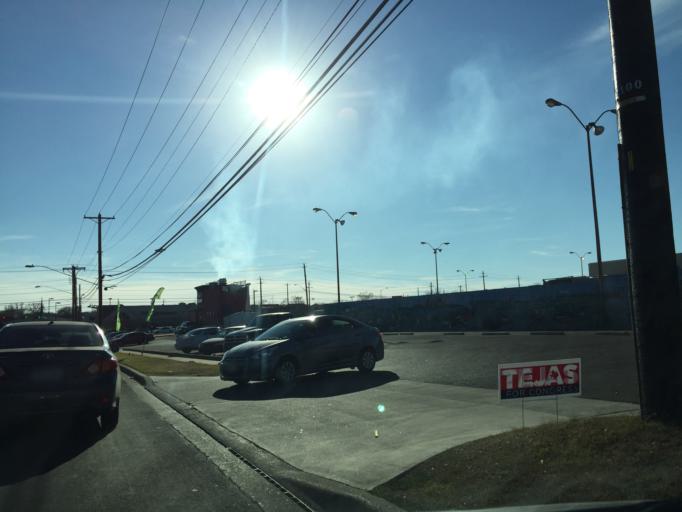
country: US
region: Texas
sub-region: Travis County
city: Rollingwood
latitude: 30.2094
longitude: -97.7808
